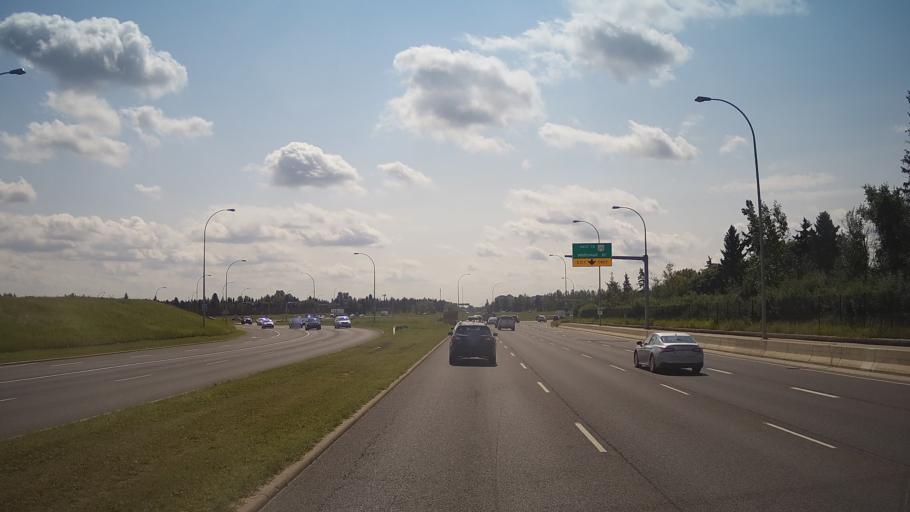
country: CA
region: Alberta
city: St. Albert
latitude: 53.5151
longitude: -113.6154
